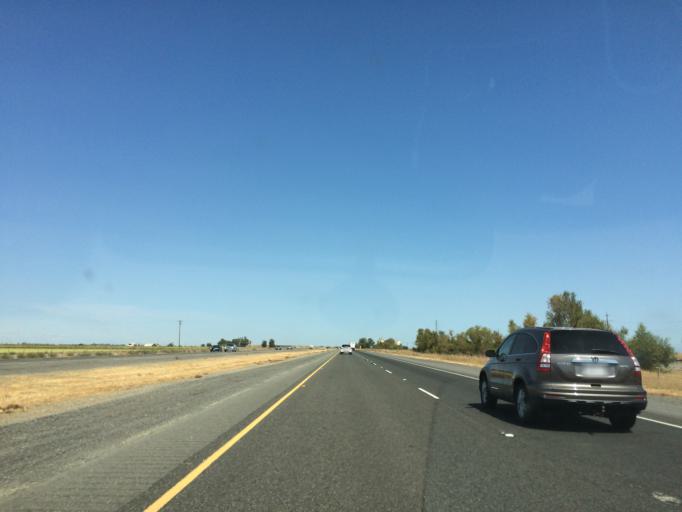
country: US
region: California
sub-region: Glenn County
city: Willows
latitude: 39.4486
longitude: -122.1934
